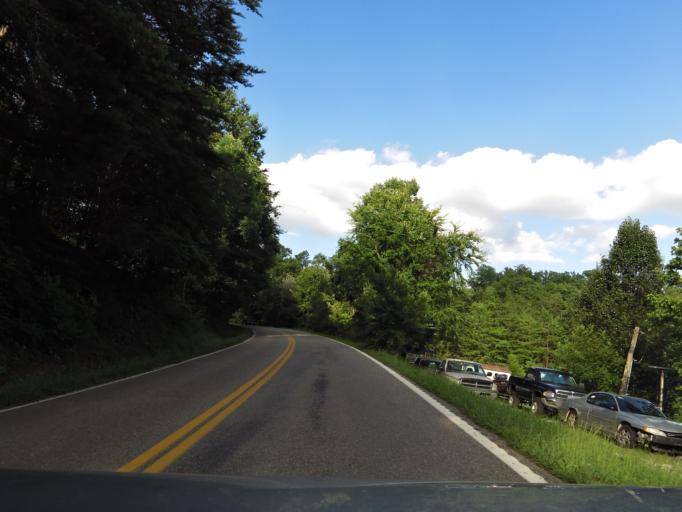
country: US
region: Tennessee
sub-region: Loudon County
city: Greenback
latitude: 35.6030
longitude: -84.0802
